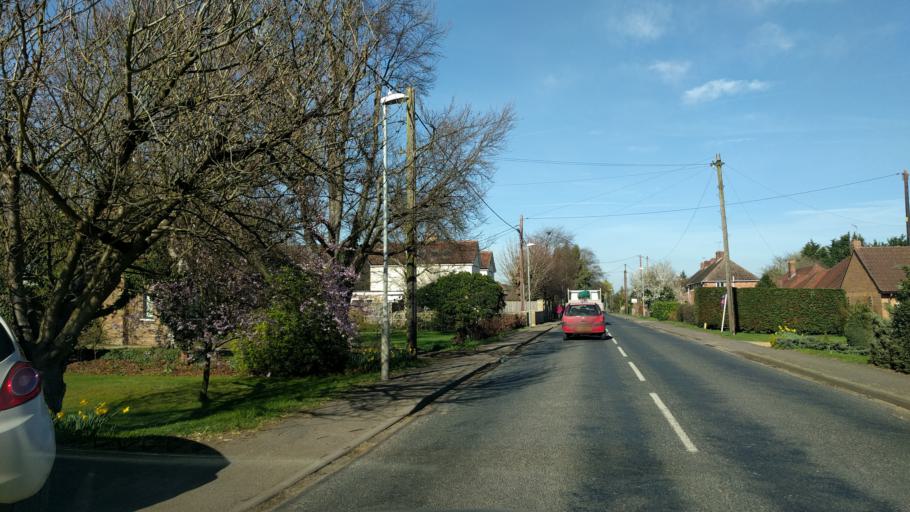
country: GB
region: England
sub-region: Cambridgeshire
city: Earith
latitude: 52.3177
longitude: 0.0590
